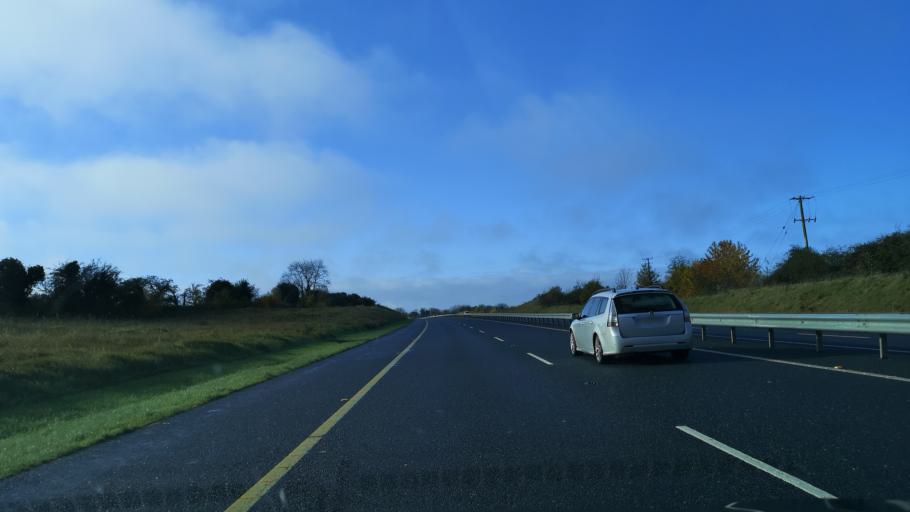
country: IE
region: Connaught
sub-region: County Galway
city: Ballinasloe
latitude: 53.3422
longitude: -8.0964
